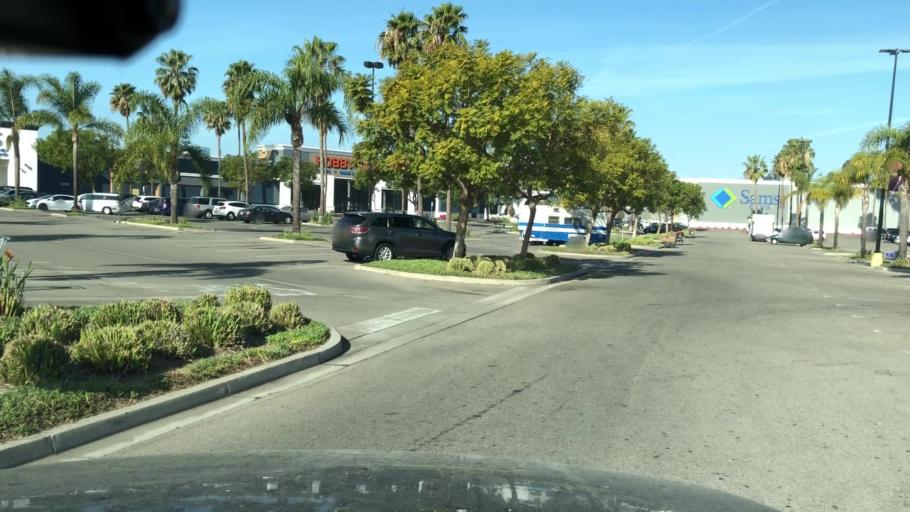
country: US
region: California
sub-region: Ventura County
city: El Rio
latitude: 34.2224
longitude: -119.1603
